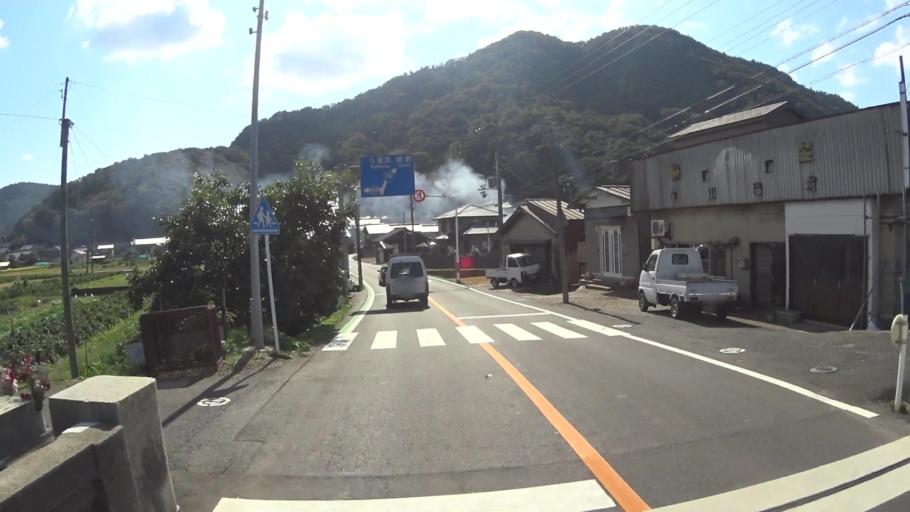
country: JP
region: Kyoto
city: Miyazu
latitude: 35.7483
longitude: 135.1650
